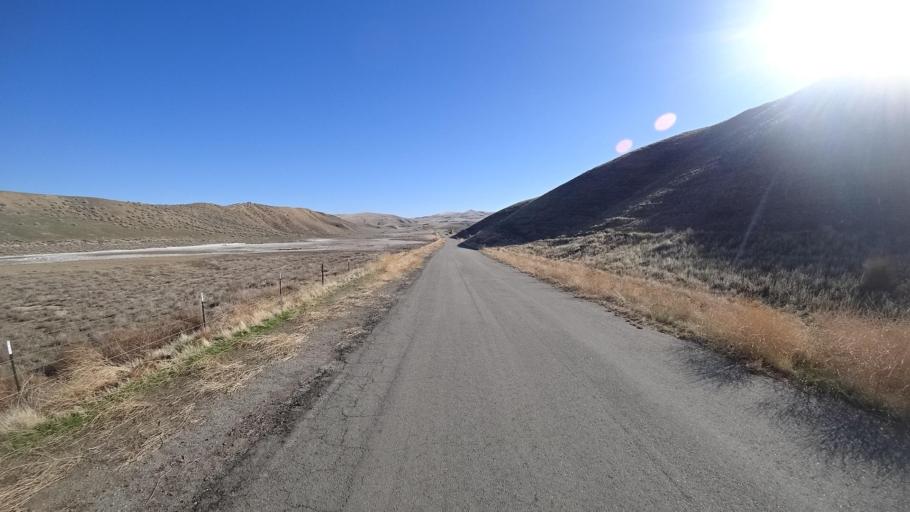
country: US
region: California
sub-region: Kern County
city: Maricopa
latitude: 34.9761
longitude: -119.4622
